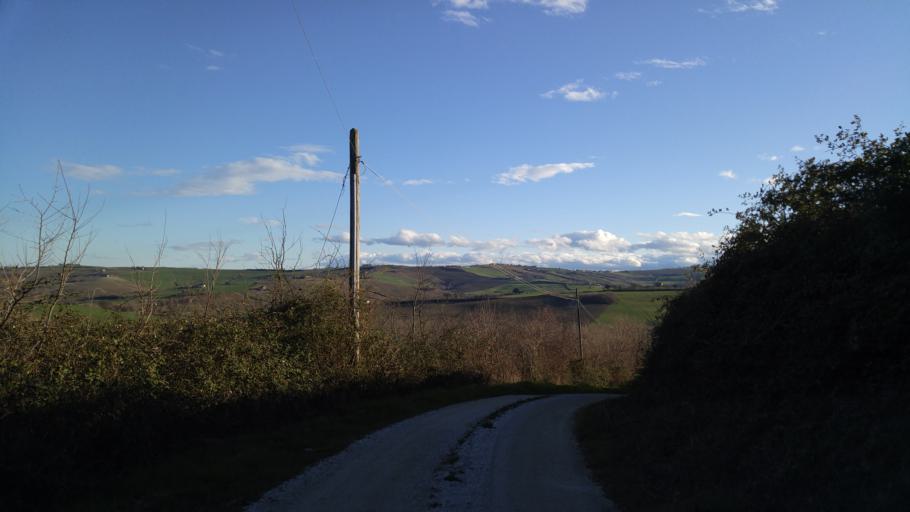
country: IT
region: The Marches
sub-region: Provincia di Pesaro e Urbino
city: San Costanzo
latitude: 43.7492
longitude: 13.0270
